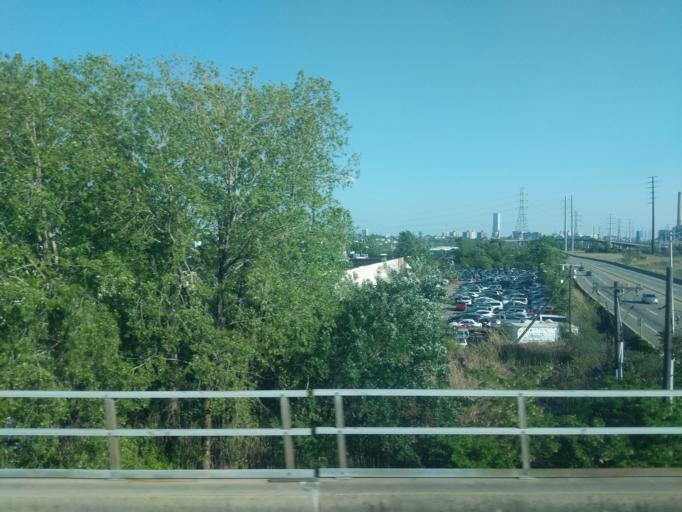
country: US
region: New Jersey
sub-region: Hudson County
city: Secaucus
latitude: 40.7626
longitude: -74.0726
